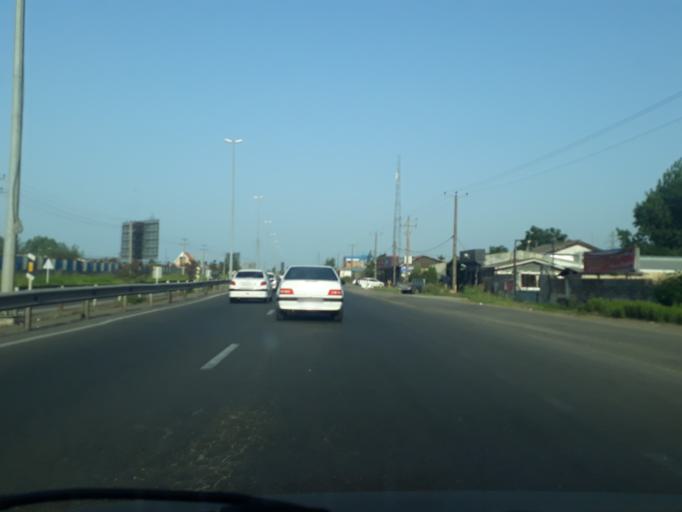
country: IR
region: Gilan
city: Bandar-e Anzali
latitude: 37.4597
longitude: 49.5828
